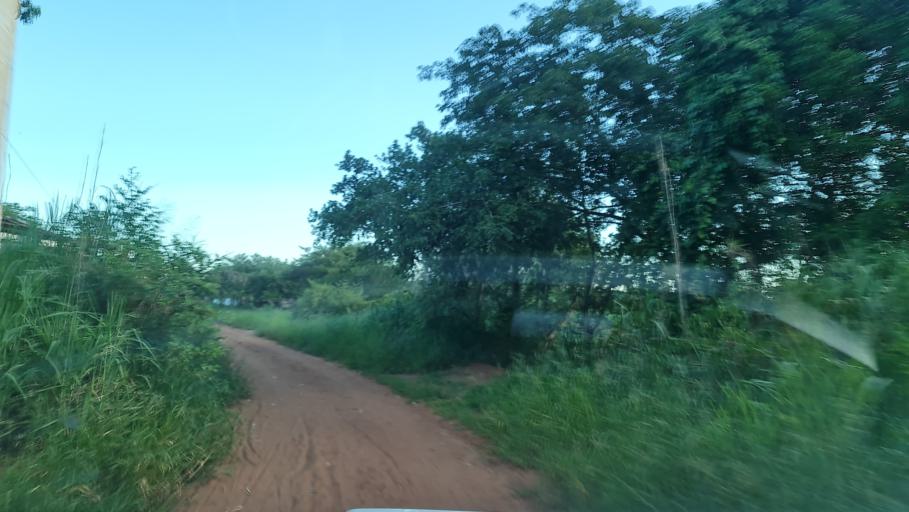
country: MZ
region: Nampula
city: Ilha de Mocambique
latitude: -14.9860
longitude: 40.0948
